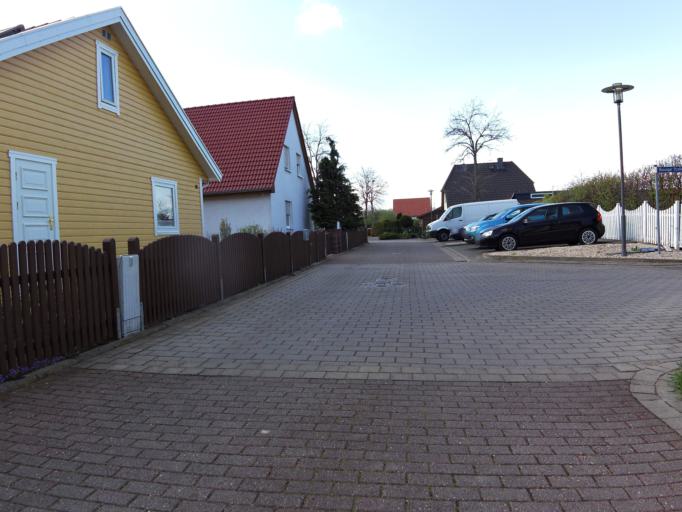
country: DE
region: Saxony
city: Markranstadt
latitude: 51.3261
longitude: 12.2789
